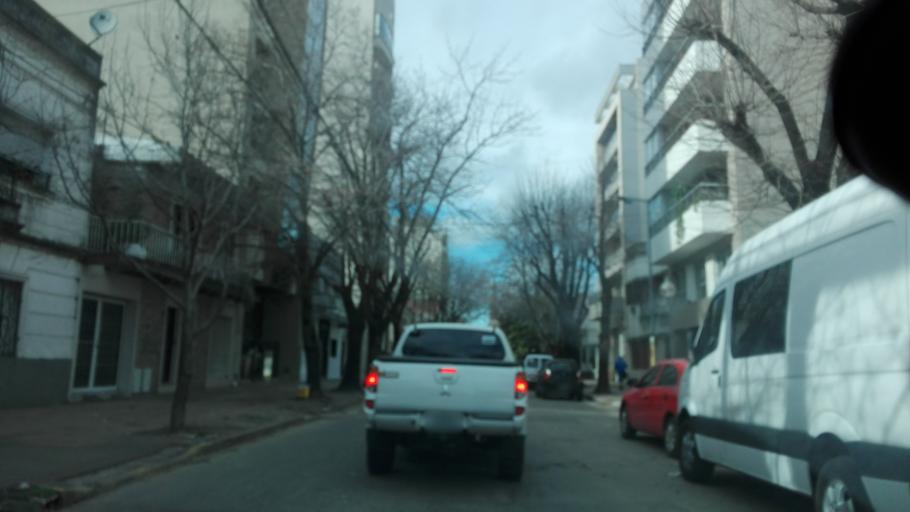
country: AR
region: Buenos Aires
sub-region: Partido de La Plata
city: La Plata
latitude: -34.9165
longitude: -57.9636
